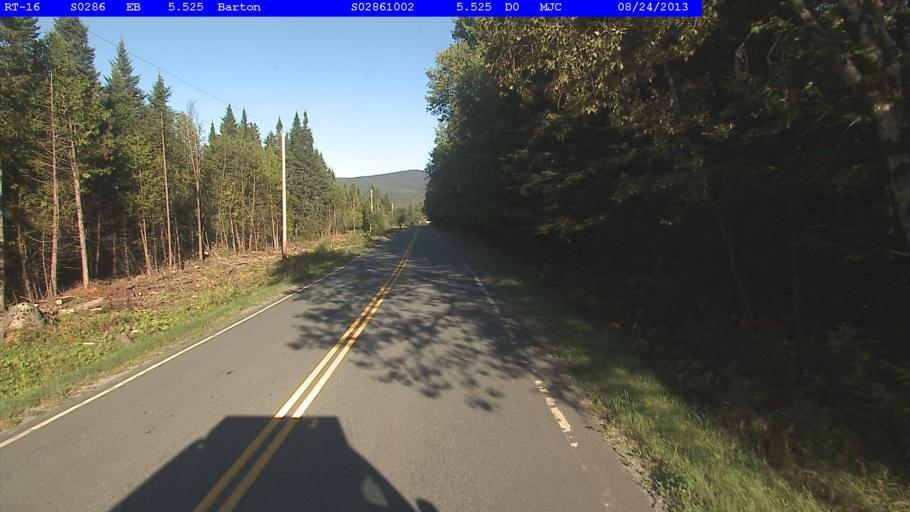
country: US
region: Vermont
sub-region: Orleans County
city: Newport
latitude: 44.7830
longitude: -72.0981
